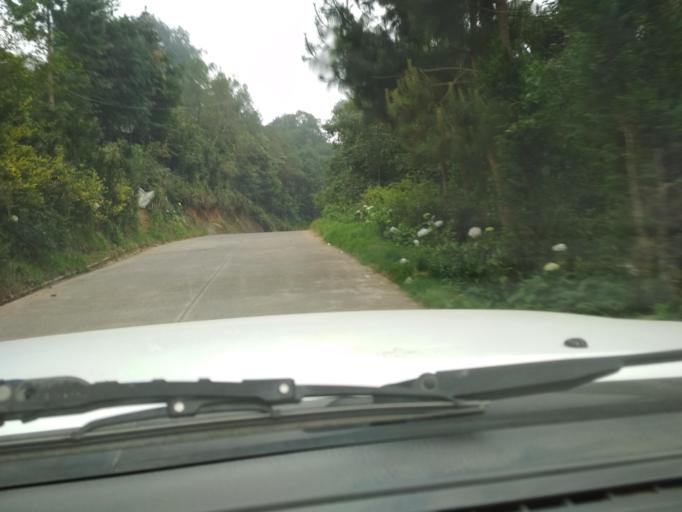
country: MX
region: Veracruz
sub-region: La Perla
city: Chilapa
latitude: 18.9747
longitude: -97.1612
